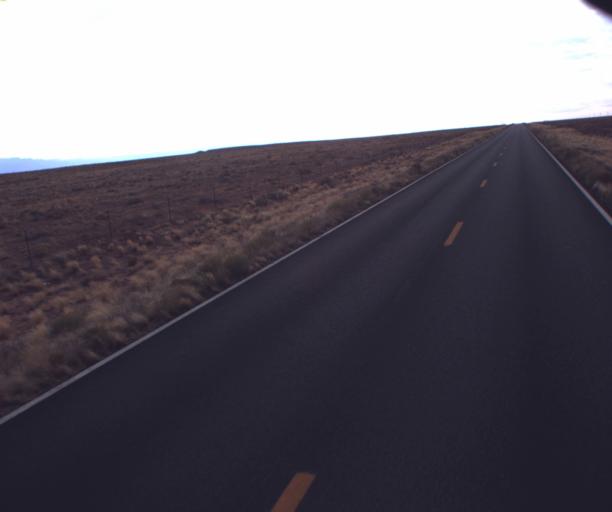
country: US
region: Arizona
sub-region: Apache County
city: Many Farms
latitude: 36.5746
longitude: -109.5504
